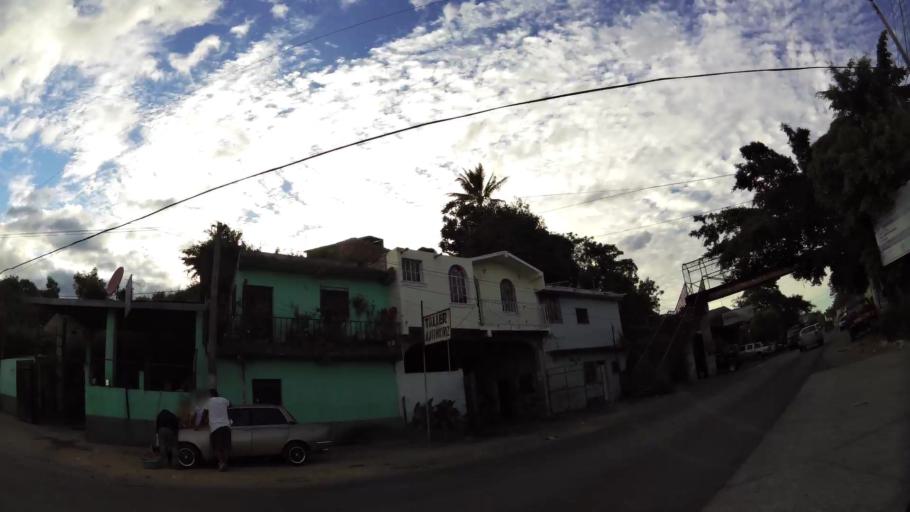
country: SV
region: Cuscatlan
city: Cojutepeque
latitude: 13.7235
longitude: -88.9311
